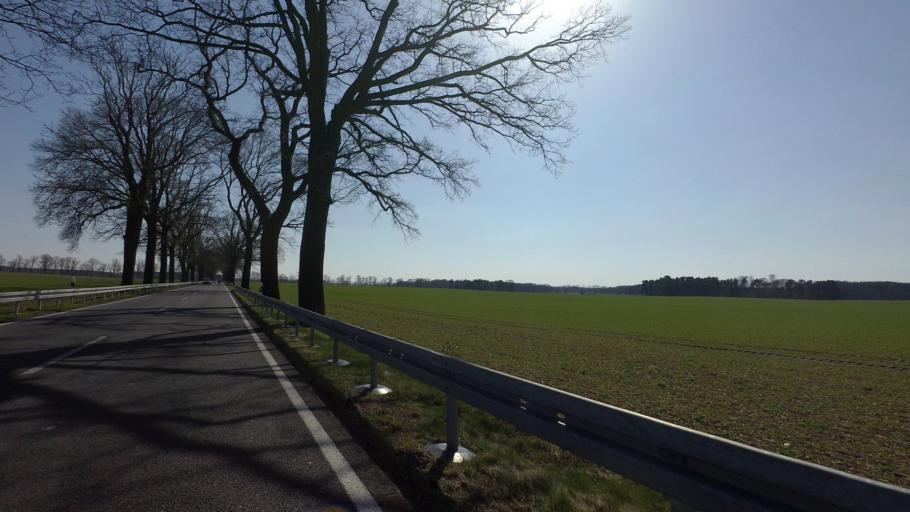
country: DE
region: Brandenburg
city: Gransee
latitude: 52.9362
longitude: 13.1539
